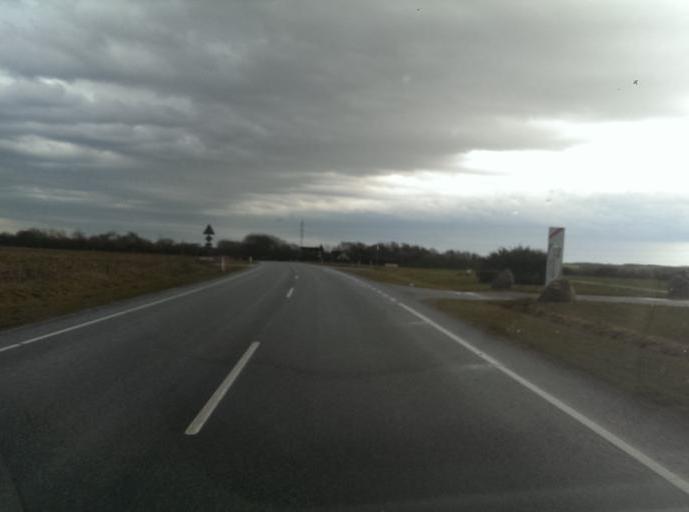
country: DK
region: South Denmark
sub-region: Esbjerg Kommune
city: Tjaereborg
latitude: 55.5090
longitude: 8.5964
